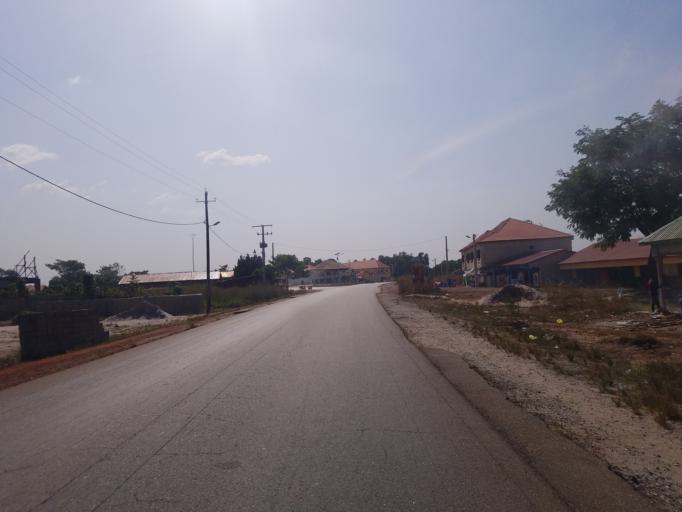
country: GN
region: Boke
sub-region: Fria
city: Fria
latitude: 10.0745
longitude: -13.7040
